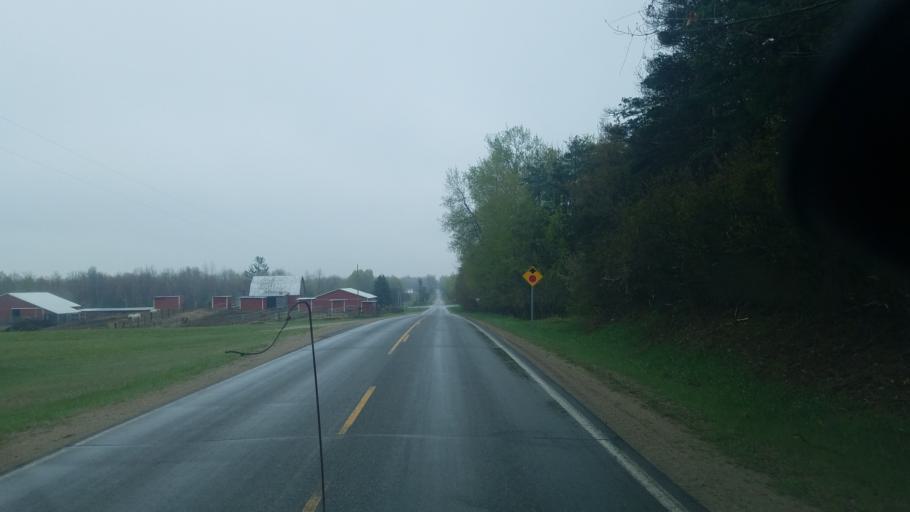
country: US
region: Michigan
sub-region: Mecosta County
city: Canadian Lakes
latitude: 43.5792
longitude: -85.3935
